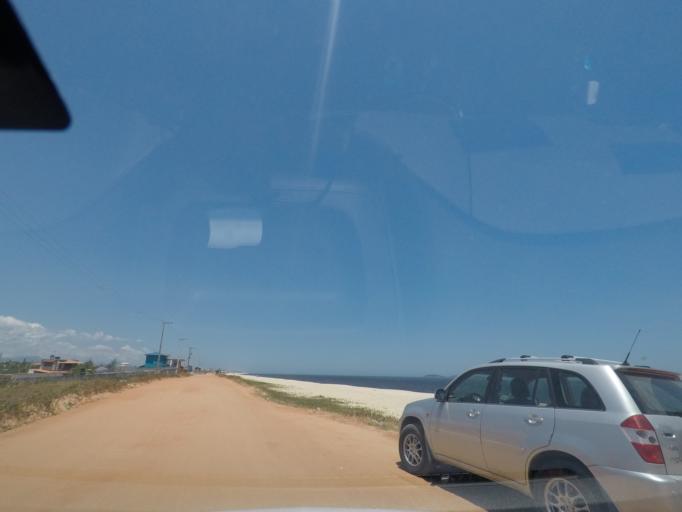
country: BR
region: Rio de Janeiro
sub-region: Niteroi
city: Niteroi
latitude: -22.9692
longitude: -42.9757
